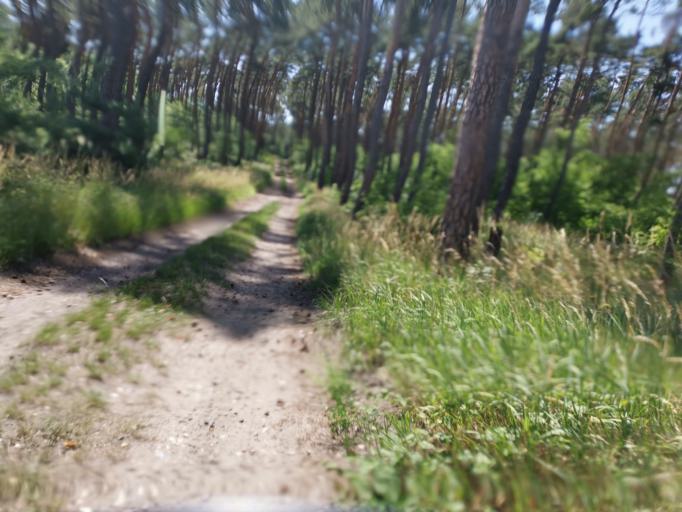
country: CZ
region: South Moravian
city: Rohatec
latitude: 48.8985
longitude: 17.2017
